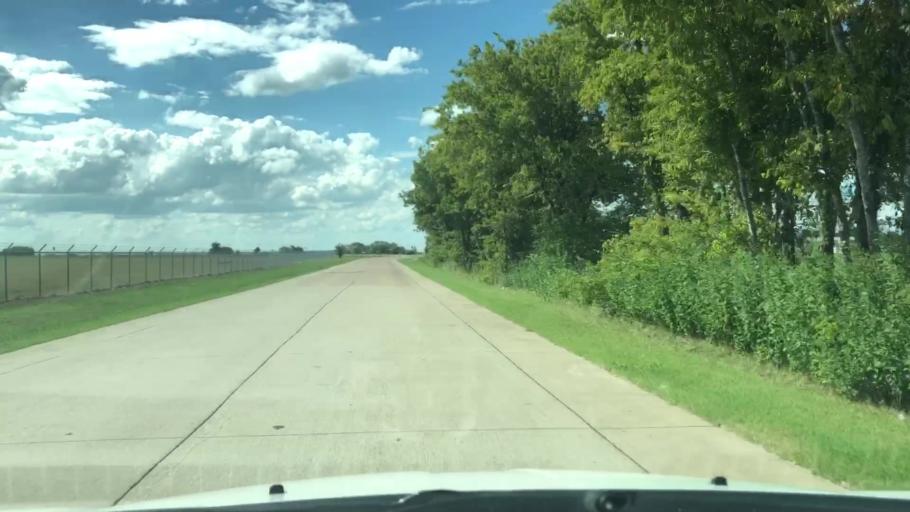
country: US
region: Texas
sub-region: Navarro County
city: Corsicana
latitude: 32.0339
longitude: -96.4006
